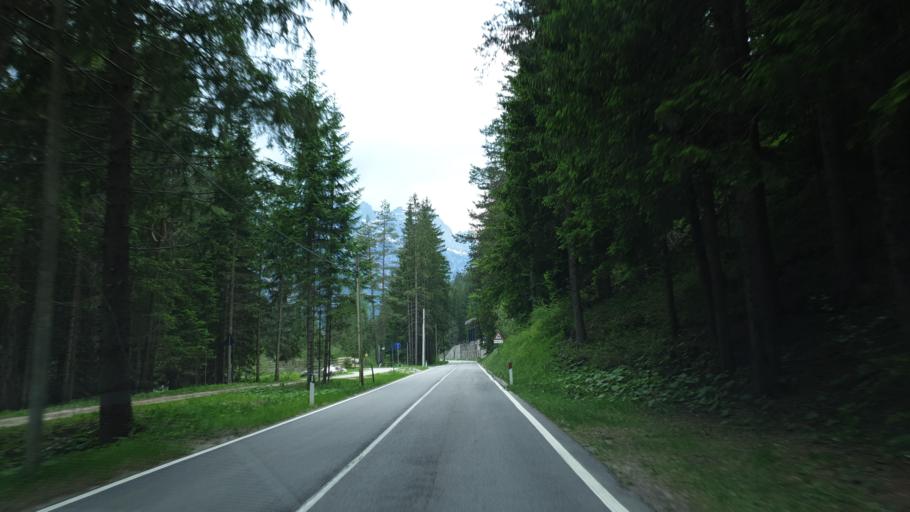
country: IT
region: Veneto
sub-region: Provincia di Belluno
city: Auronzo
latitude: 46.5631
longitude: 12.3449
